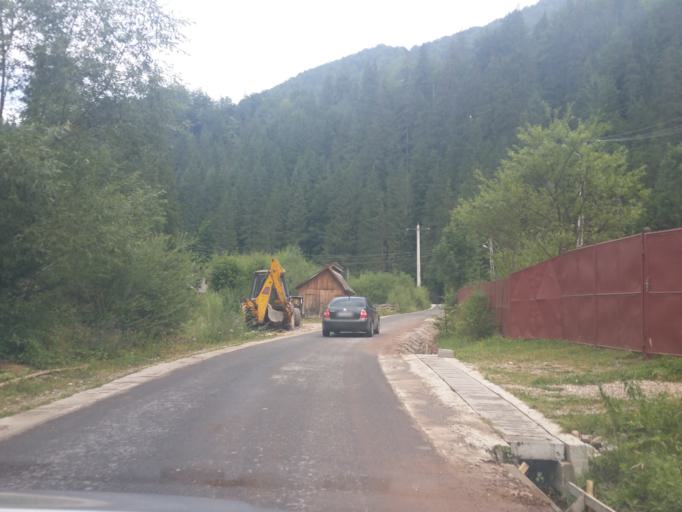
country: RO
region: Alba
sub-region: Comuna Garda de Sus
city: Garda de Sus
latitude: 46.4692
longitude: 22.8194
